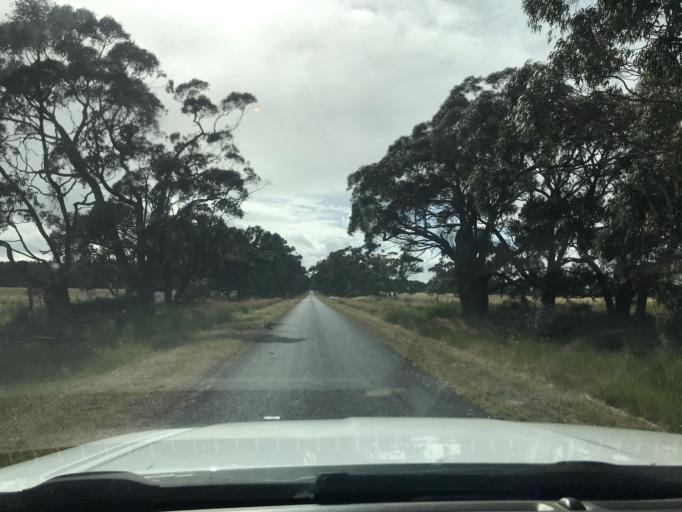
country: AU
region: South Australia
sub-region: Wattle Range
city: Penola
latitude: -37.1861
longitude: 141.2151
